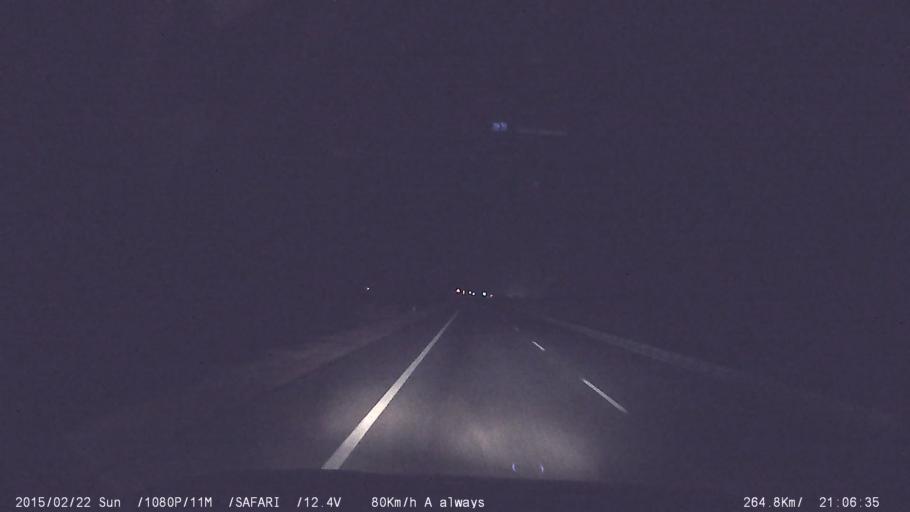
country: IN
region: Tamil Nadu
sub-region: Karur
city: Pallappatti
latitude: 10.7122
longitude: 77.9303
